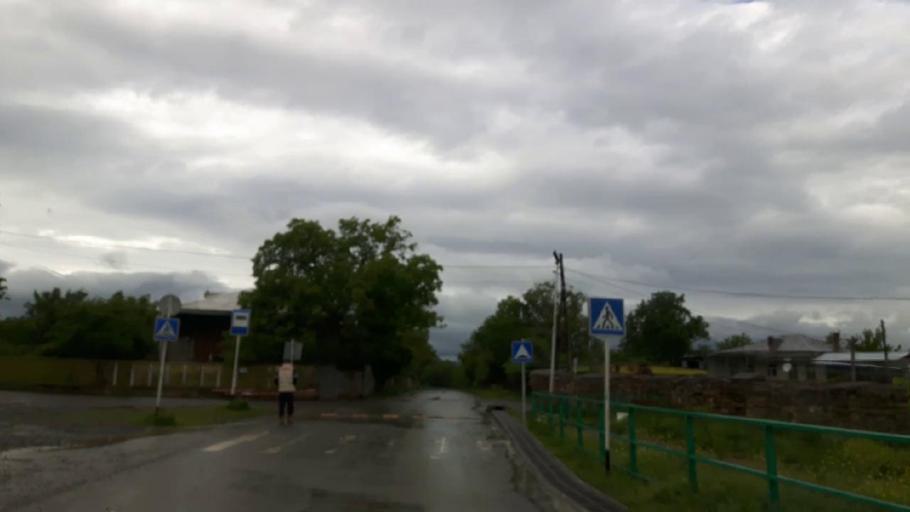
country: GE
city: Agara
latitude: 41.9942
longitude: 43.7323
